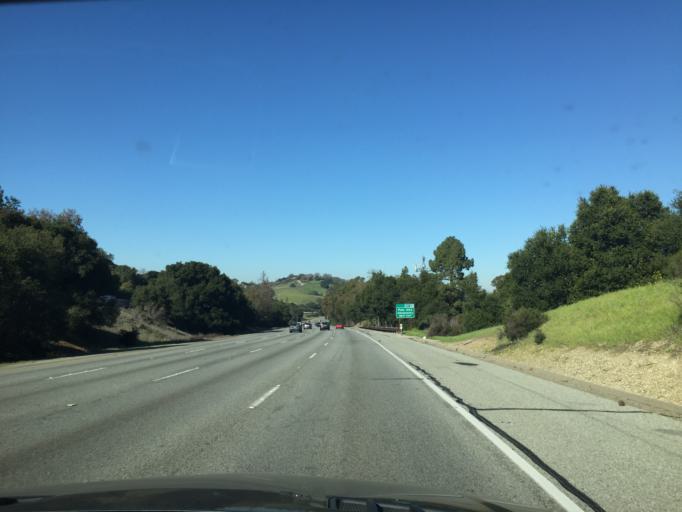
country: US
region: California
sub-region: Santa Clara County
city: Los Altos Hills
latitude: 37.3741
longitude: -122.1452
